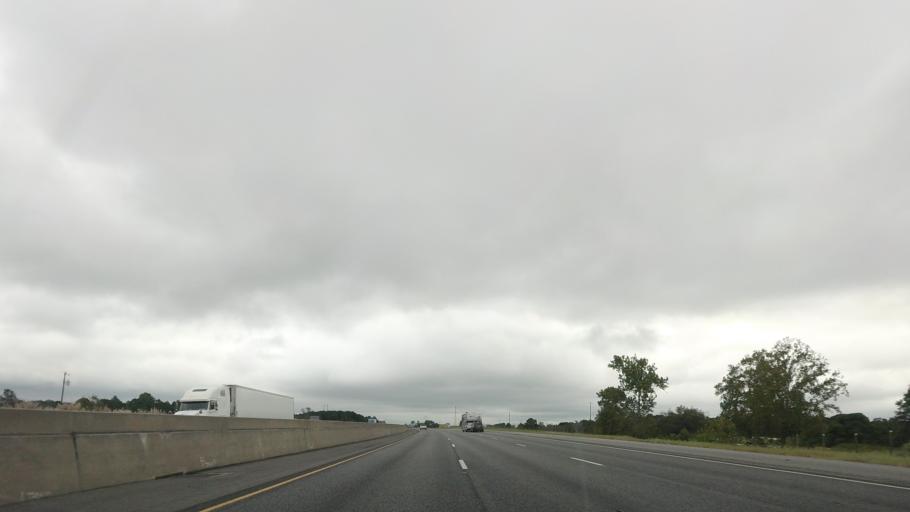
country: US
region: Georgia
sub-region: Turner County
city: Ashburn
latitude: 31.5922
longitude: -83.5586
